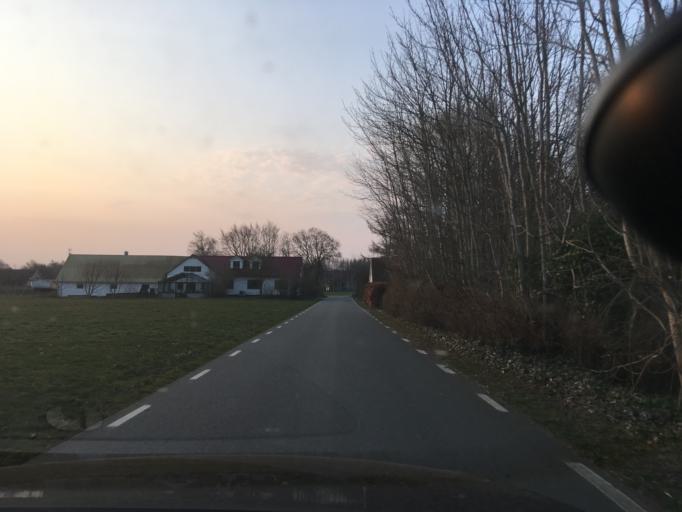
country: SE
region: Skane
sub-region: Ystads Kommun
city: Kopingebro
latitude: 55.4014
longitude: 14.1632
